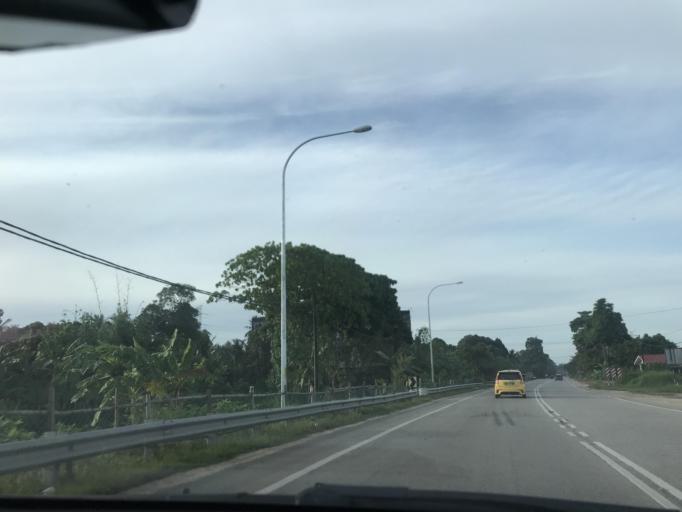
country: MY
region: Kelantan
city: Kampung Lemal
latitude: 5.9935
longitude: 102.1887
